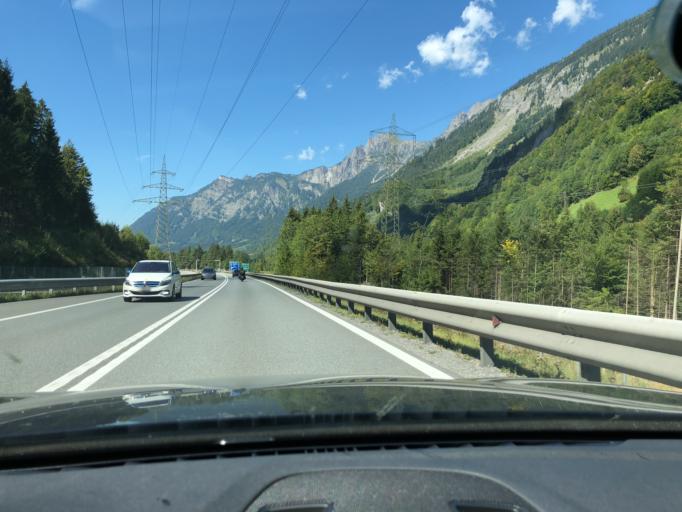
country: AT
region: Vorarlberg
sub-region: Politischer Bezirk Bludenz
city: Dalaas
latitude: 47.1316
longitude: 9.9535
